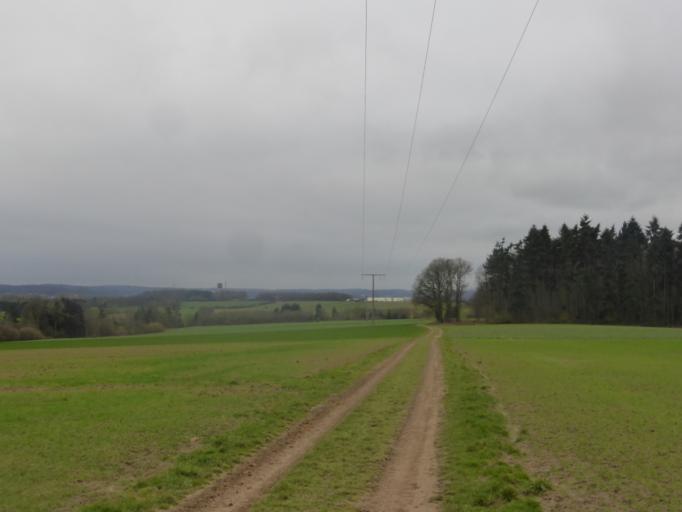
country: LU
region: Luxembourg
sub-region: Canton d'Esch-sur-Alzette
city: Leudelange
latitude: 49.5487
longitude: 6.0585
